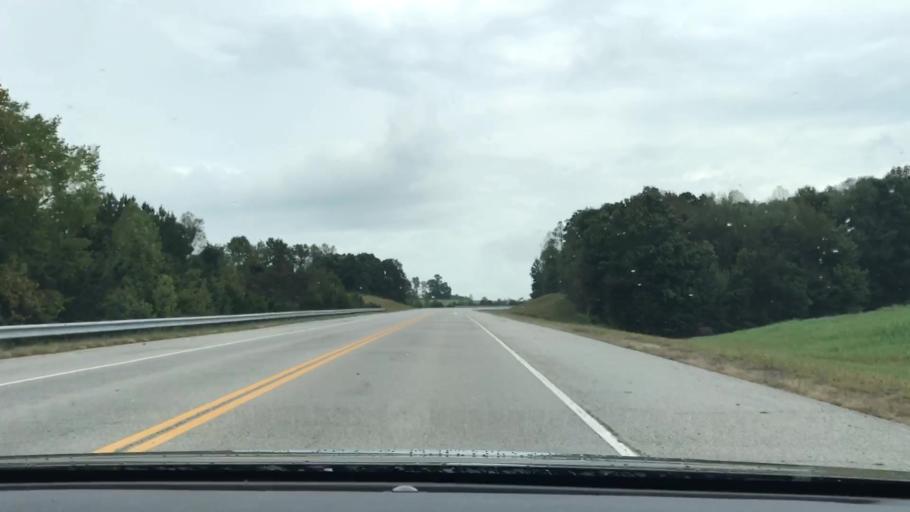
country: US
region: Tennessee
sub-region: Macon County
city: Red Boiling Springs
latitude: 36.5362
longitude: -85.8243
